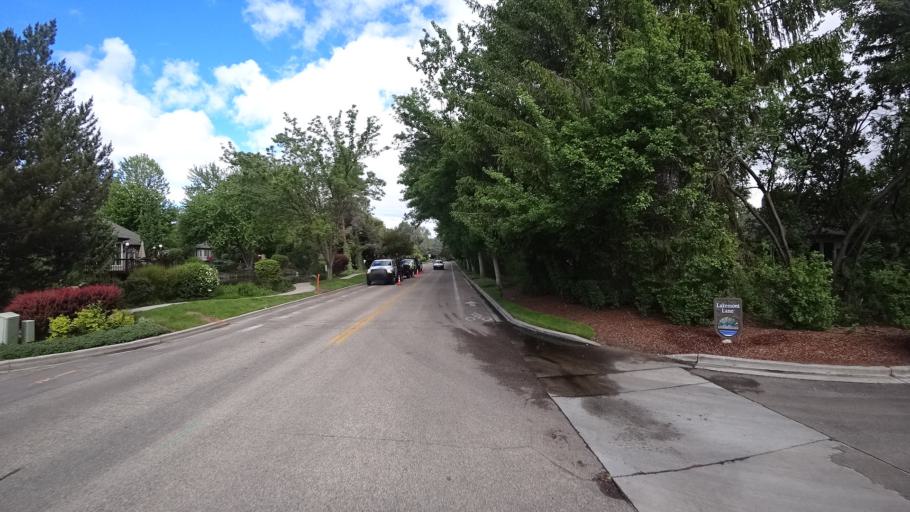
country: US
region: Idaho
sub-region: Ada County
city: Eagle
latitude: 43.6667
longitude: -116.2953
